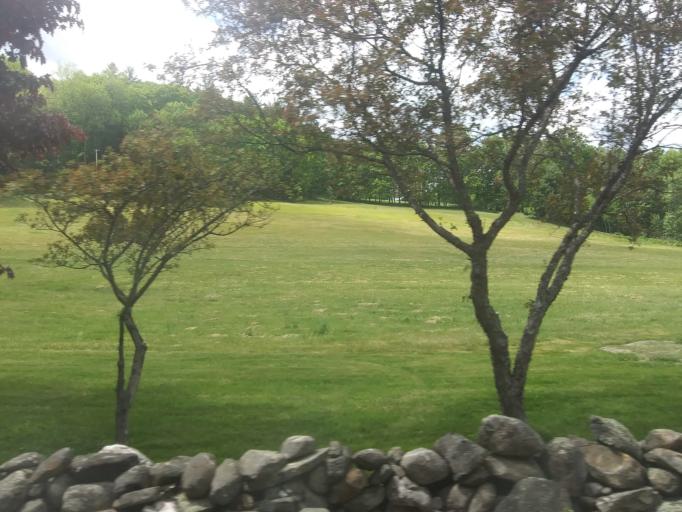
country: US
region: Massachusetts
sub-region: Franklin County
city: Shelburne Falls
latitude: 42.5926
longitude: -72.7639
